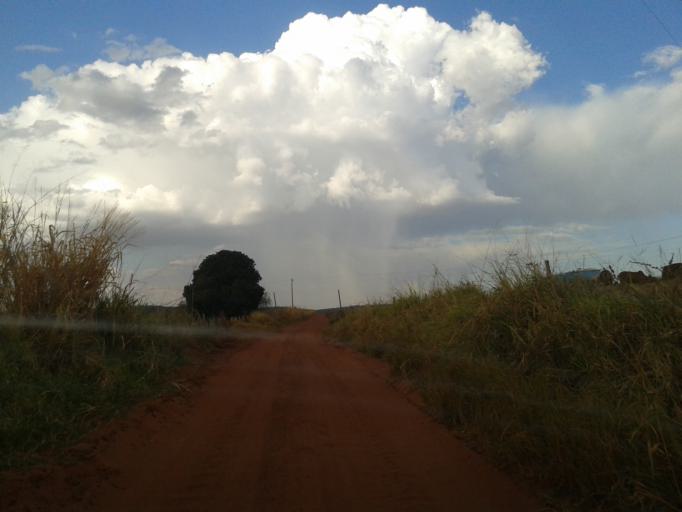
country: BR
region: Minas Gerais
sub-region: Santa Vitoria
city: Santa Vitoria
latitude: -19.1987
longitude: -49.9327
